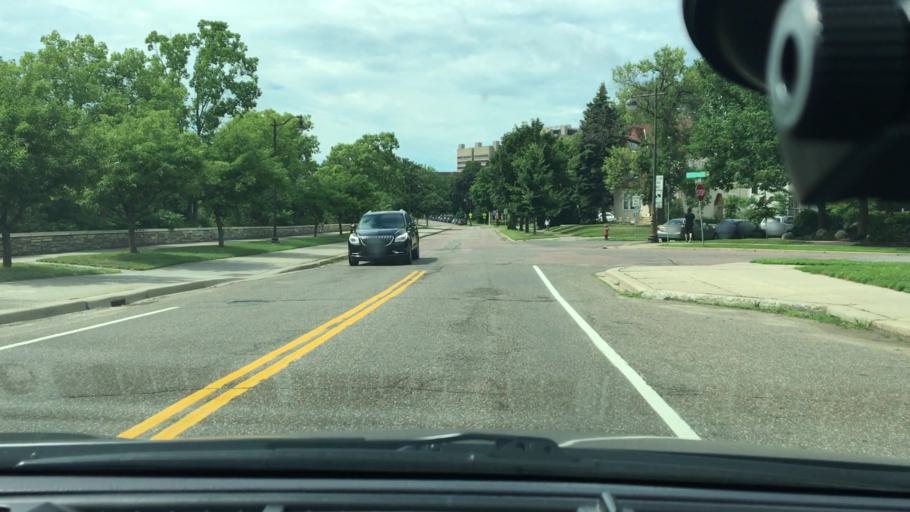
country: US
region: Minnesota
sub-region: Ramsey County
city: Lauderdale
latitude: 44.9676
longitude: -93.2254
